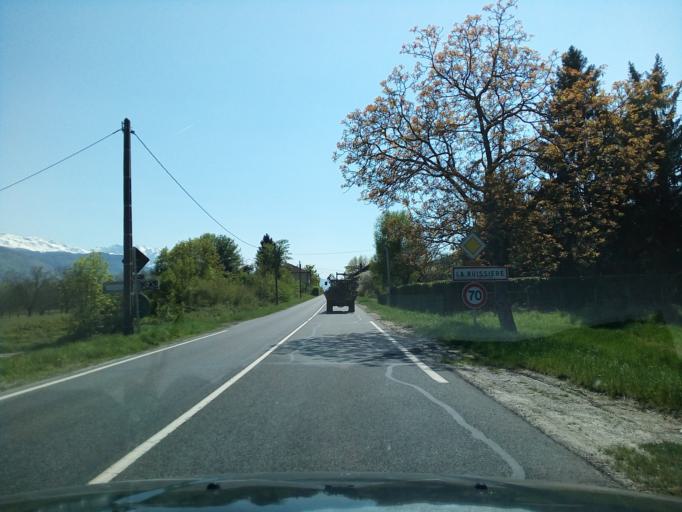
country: FR
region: Rhone-Alpes
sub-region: Departement de l'Isere
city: Barraux
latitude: 45.4058
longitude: 5.9809
